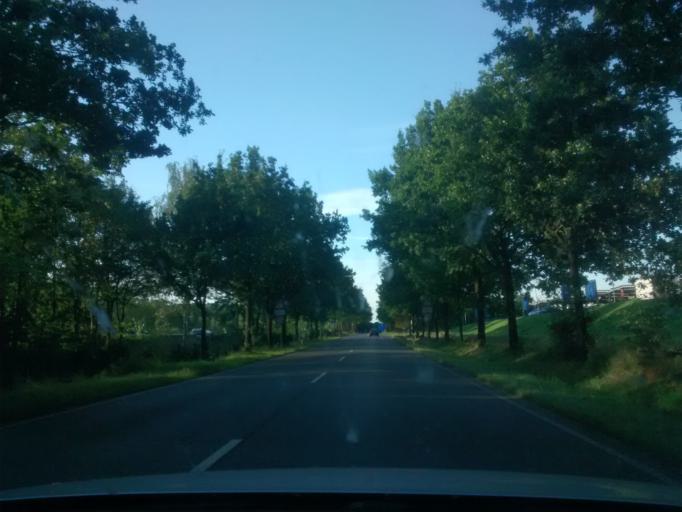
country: DE
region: Hesse
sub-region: Regierungsbezirk Kassel
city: Fuldabruck
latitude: 51.2799
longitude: 9.4953
